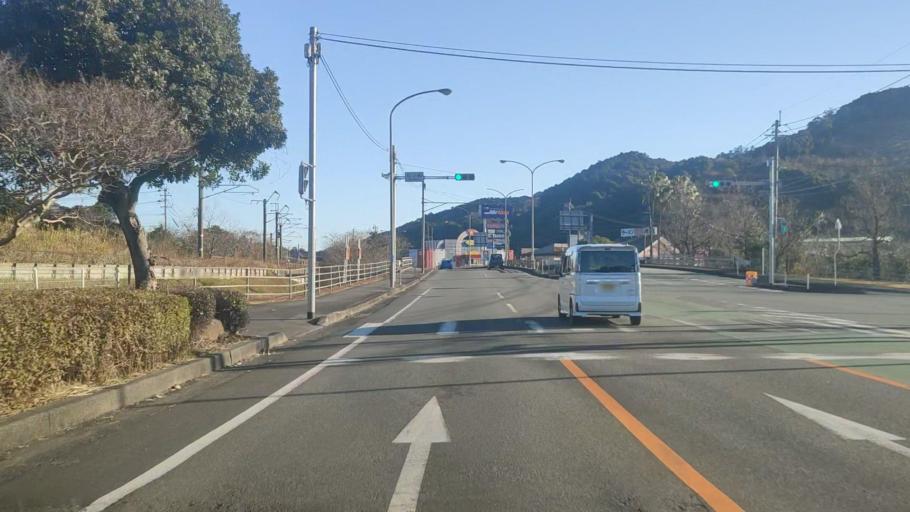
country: JP
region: Miyazaki
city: Nobeoka
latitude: 32.4492
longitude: 131.6378
